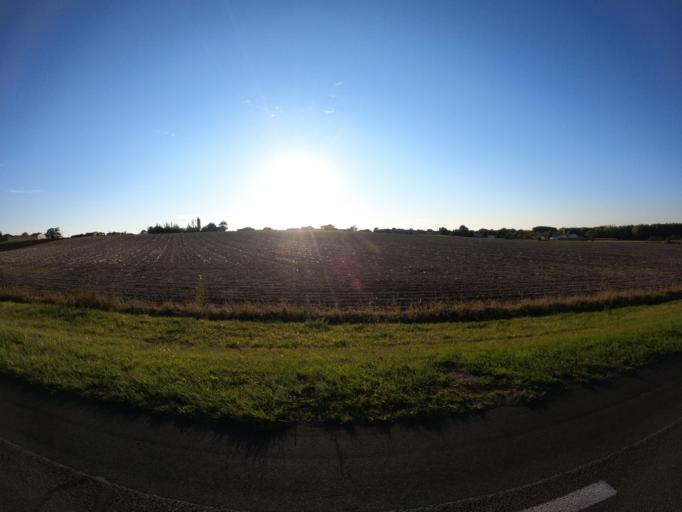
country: FR
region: Pays de la Loire
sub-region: Departement de la Vendee
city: Sainte-Hermine
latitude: 46.5533
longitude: -1.0411
